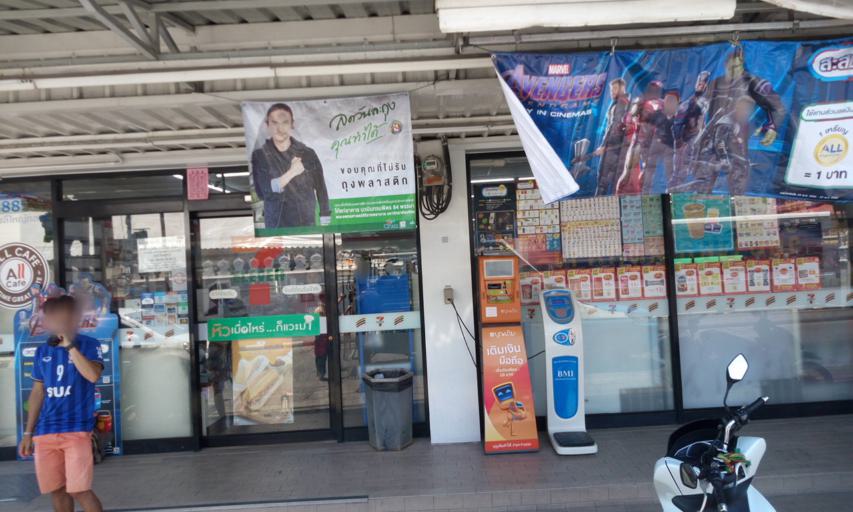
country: TH
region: Bangkok
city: Bang Na
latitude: 13.6093
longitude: 100.7048
